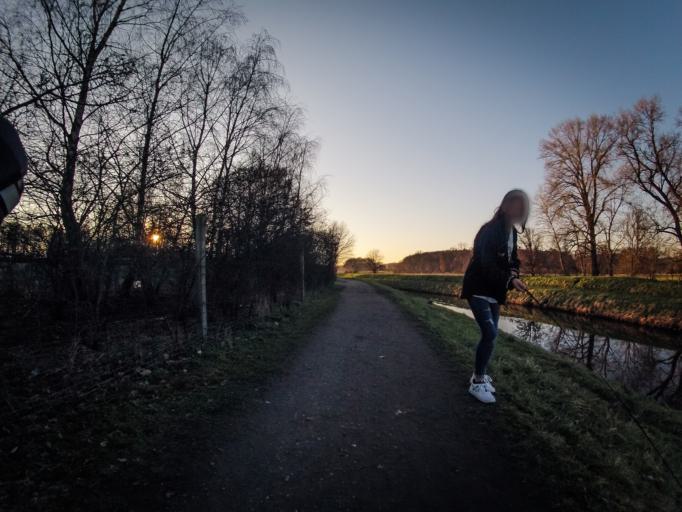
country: DE
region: Lower Saxony
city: Wallenhorst
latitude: 52.3101
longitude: 7.9940
